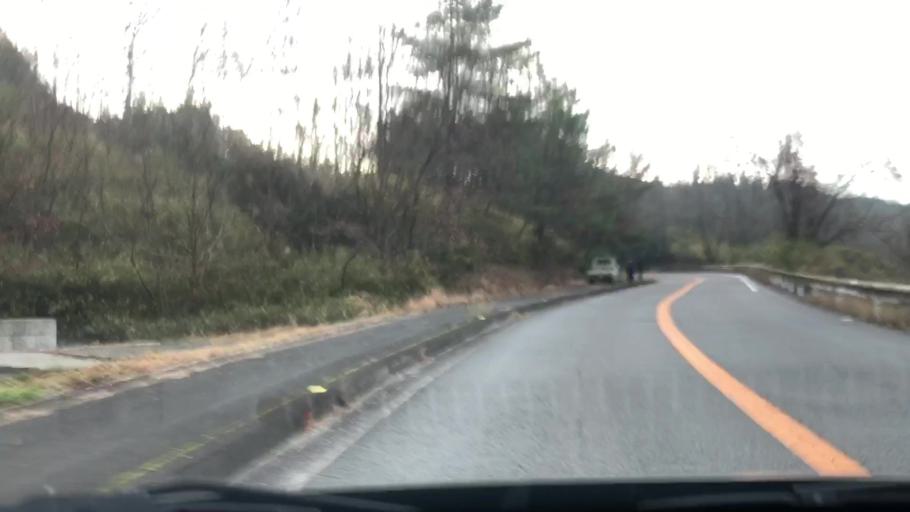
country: JP
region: Oita
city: Takedamachi
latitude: 32.9706
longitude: 131.5050
